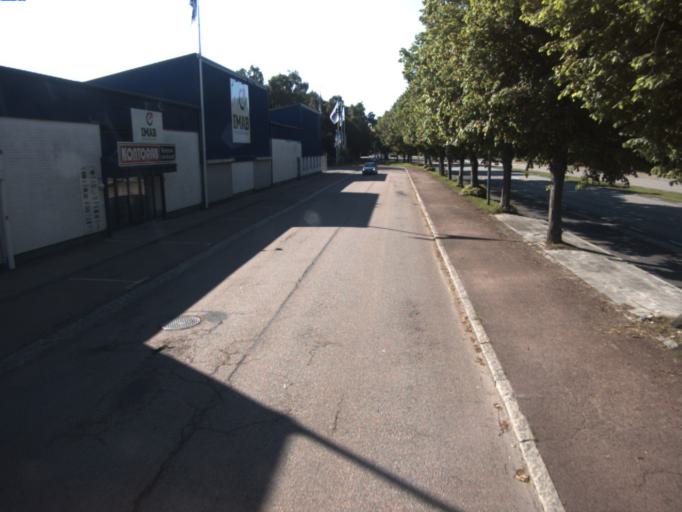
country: SE
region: Skane
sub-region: Helsingborg
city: Helsingborg
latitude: 56.0245
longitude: 12.7151
